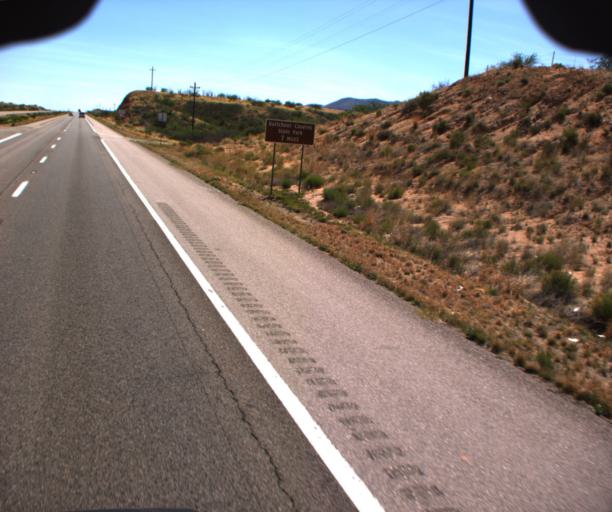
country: US
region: Arizona
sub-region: Cochise County
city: Whetstone
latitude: 31.9352
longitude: -110.3413
